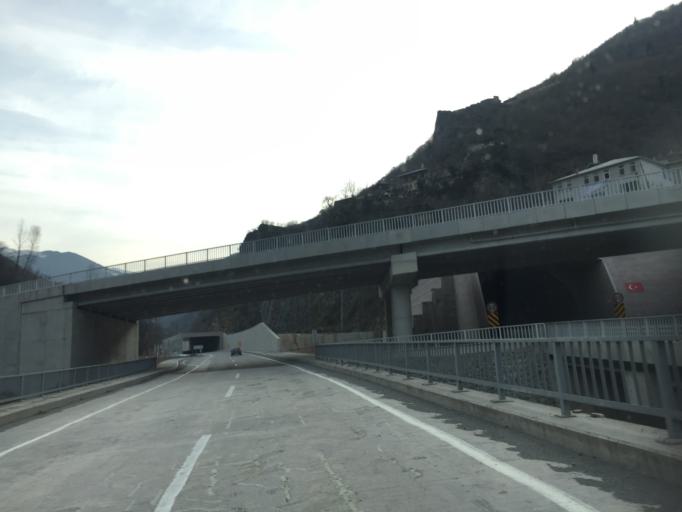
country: TR
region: Trabzon
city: Macka
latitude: 40.7793
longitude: 39.5696
